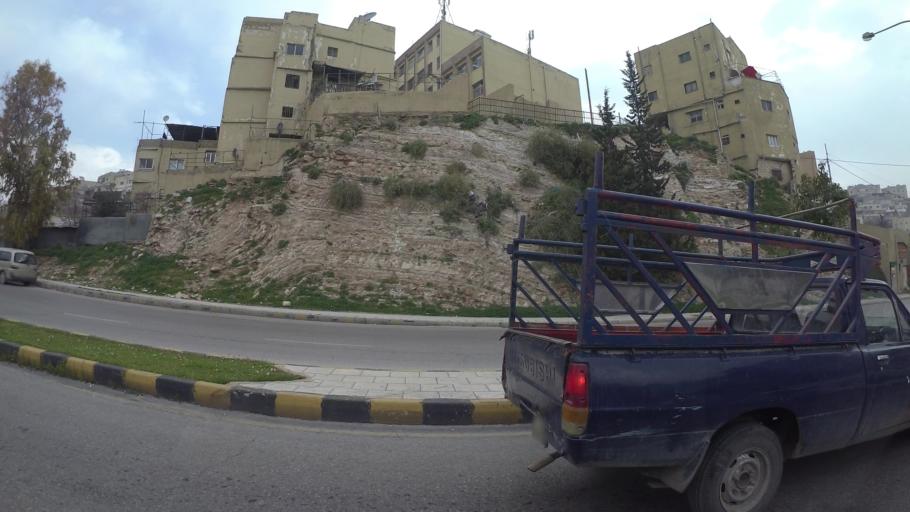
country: JO
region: Amman
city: Amman
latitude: 31.9580
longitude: 35.9351
